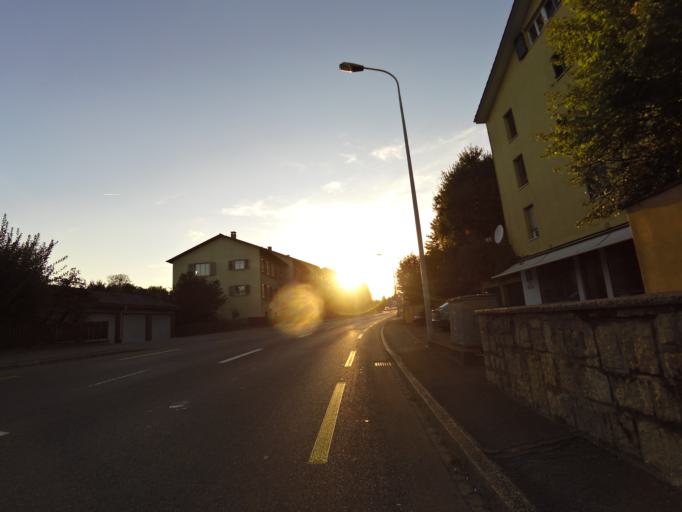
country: CH
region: Aargau
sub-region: Bezirk Aarau
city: Aarau
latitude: 47.3954
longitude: 8.0331
